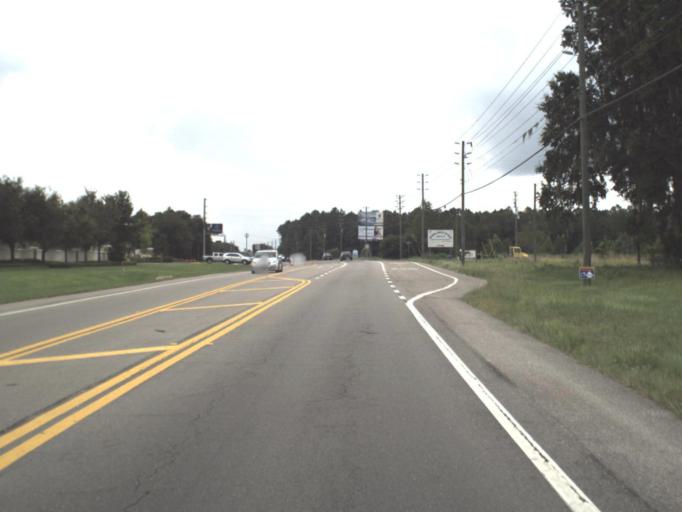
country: US
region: Florida
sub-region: Pasco County
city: Zephyrhills West
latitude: 28.2189
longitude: -82.2599
